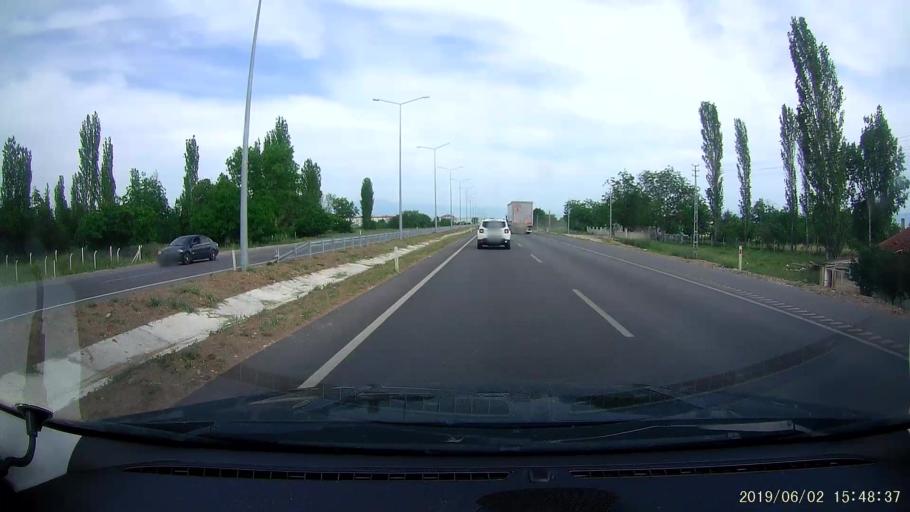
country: TR
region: Amasya
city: Merzifon
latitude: 40.8616
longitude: 35.4452
